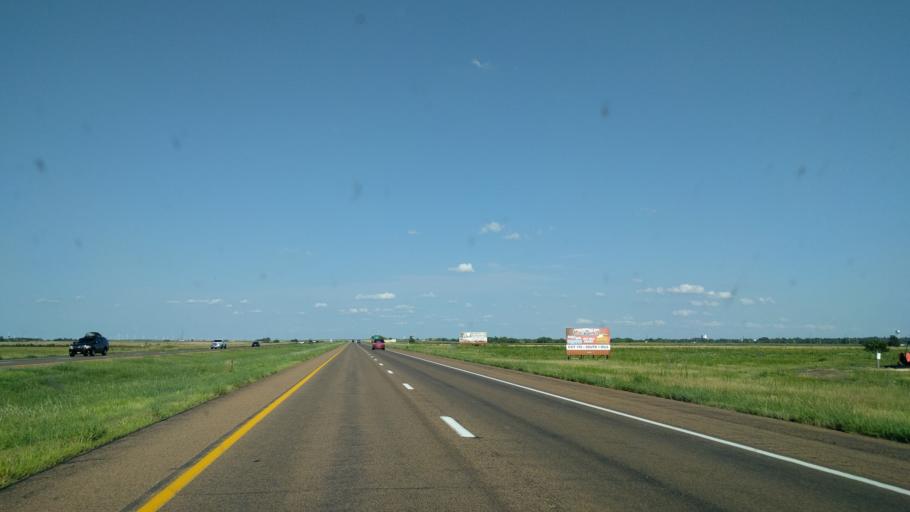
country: US
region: Kansas
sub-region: Ellis County
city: Ellis
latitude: 38.9500
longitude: -99.5886
